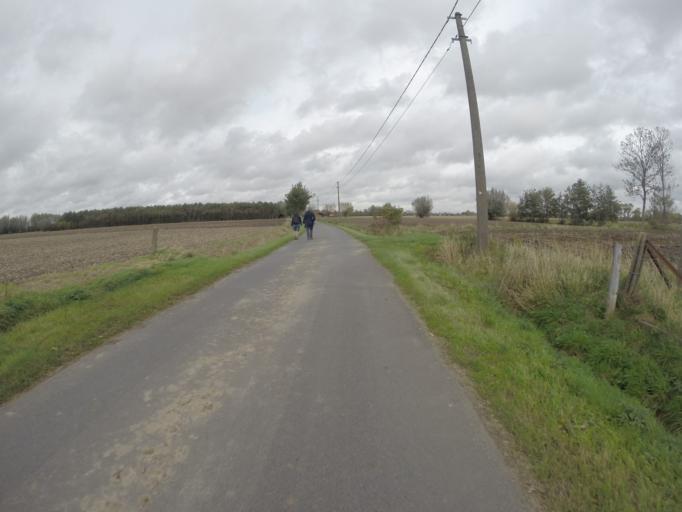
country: BE
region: Flanders
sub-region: Provincie Oost-Vlaanderen
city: Knesselare
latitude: 51.1380
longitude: 3.3895
